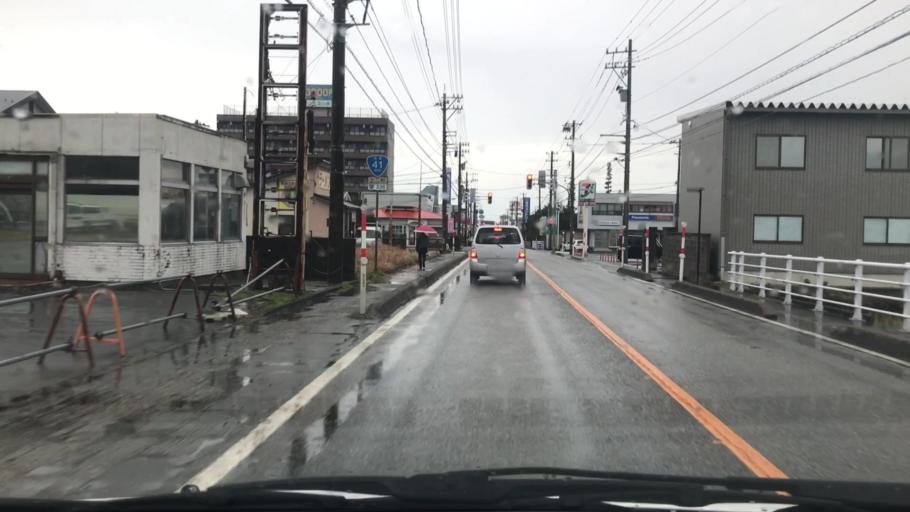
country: JP
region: Toyama
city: Yatsuomachi-higashikumisaka
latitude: 36.5886
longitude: 137.2053
